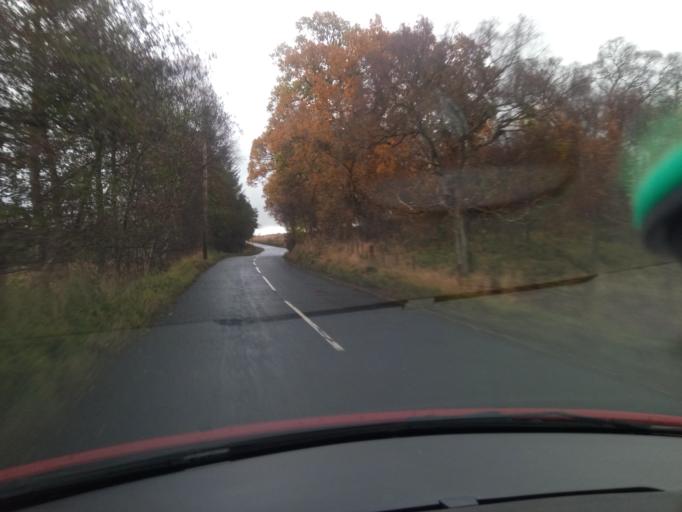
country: GB
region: England
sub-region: Northumberland
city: Birtley
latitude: 55.1351
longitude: -2.2549
